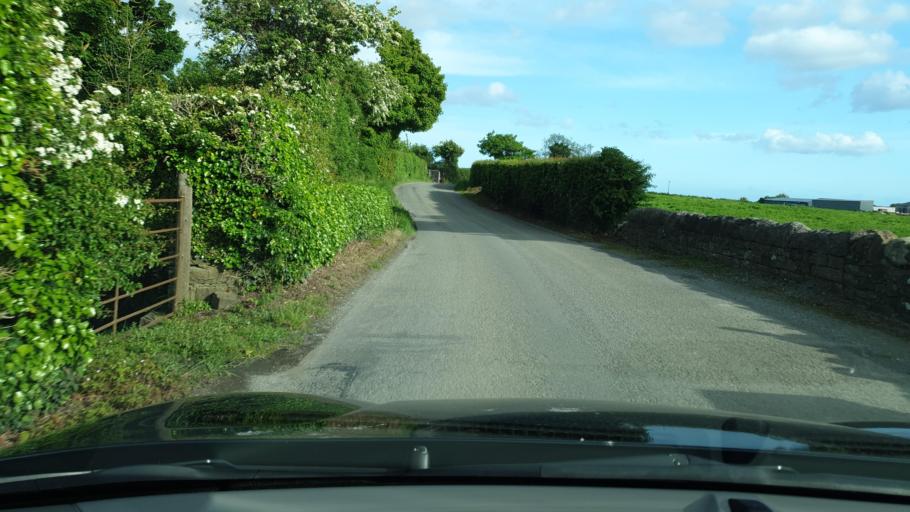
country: IE
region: Leinster
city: Balrothery
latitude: 53.5484
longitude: -6.2044
